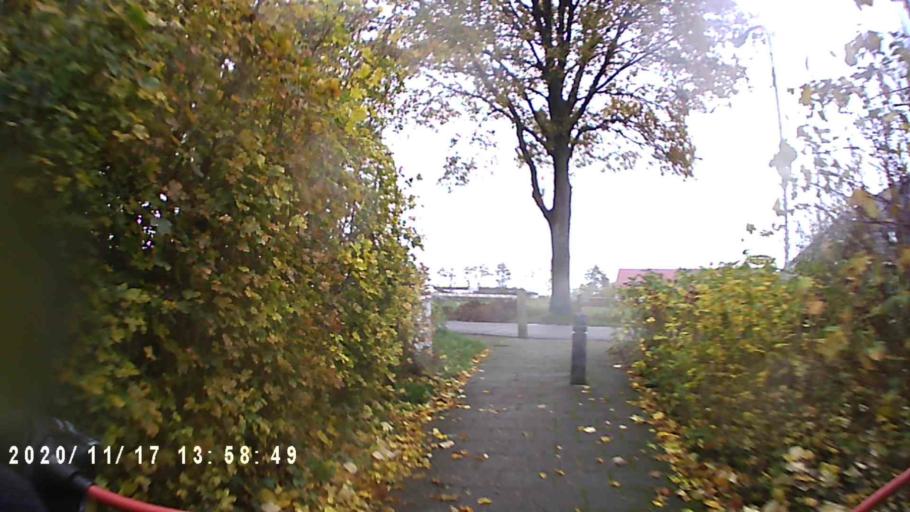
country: NL
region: Groningen
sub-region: Gemeente Zuidhorn
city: Grijpskerk
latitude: 53.2254
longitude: 6.3501
